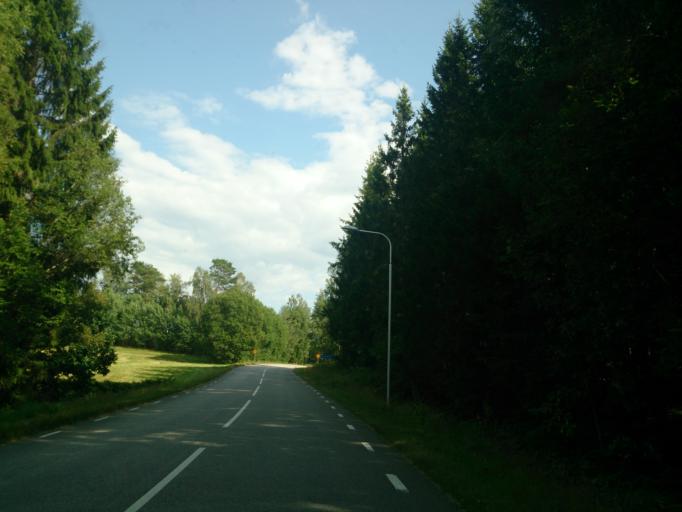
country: SE
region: Joenkoeping
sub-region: Varnamo Kommun
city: Bredaryd
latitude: 57.0945
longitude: 13.6849
